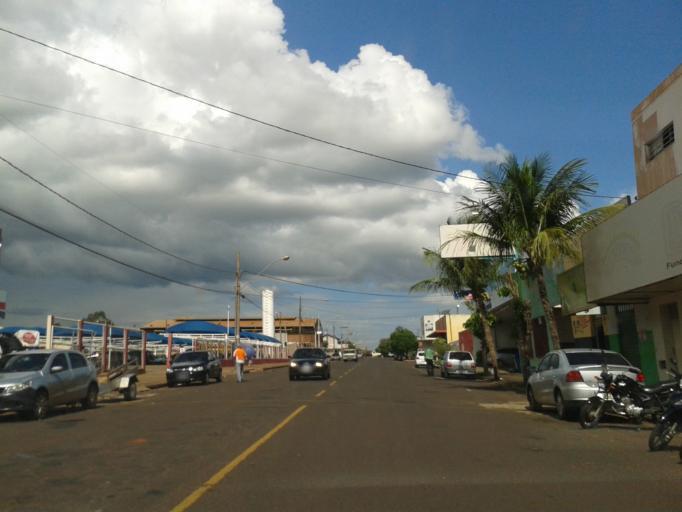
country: BR
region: Minas Gerais
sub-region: Ituiutaba
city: Ituiutaba
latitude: -18.9842
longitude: -49.4686
